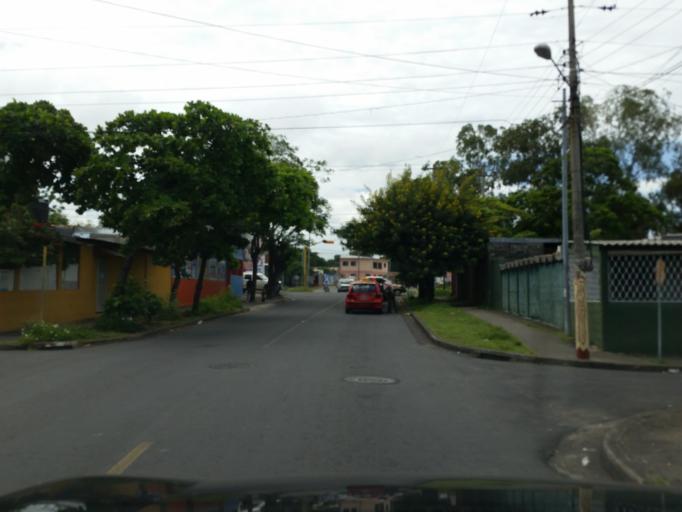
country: NI
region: Managua
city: Managua
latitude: 12.1300
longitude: -86.2452
